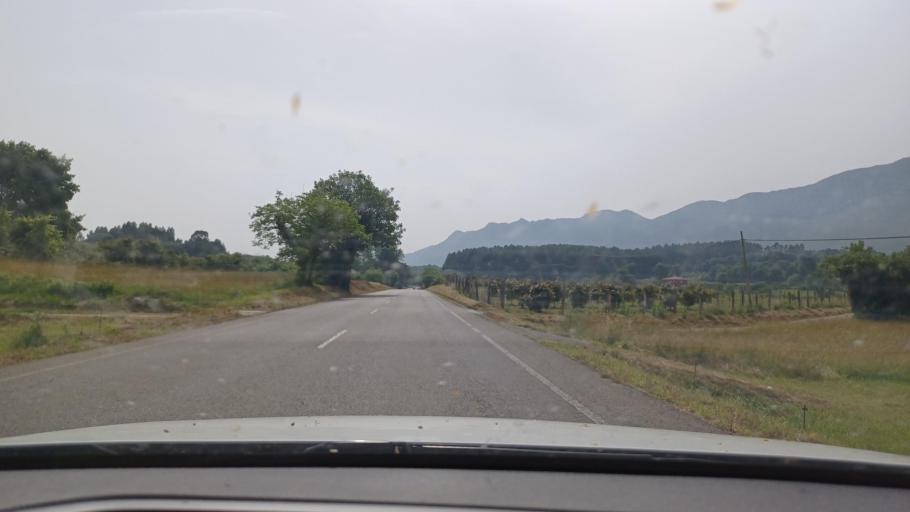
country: ES
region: Asturias
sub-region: Province of Asturias
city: Ribadesella
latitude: 43.4538
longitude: -5.0333
